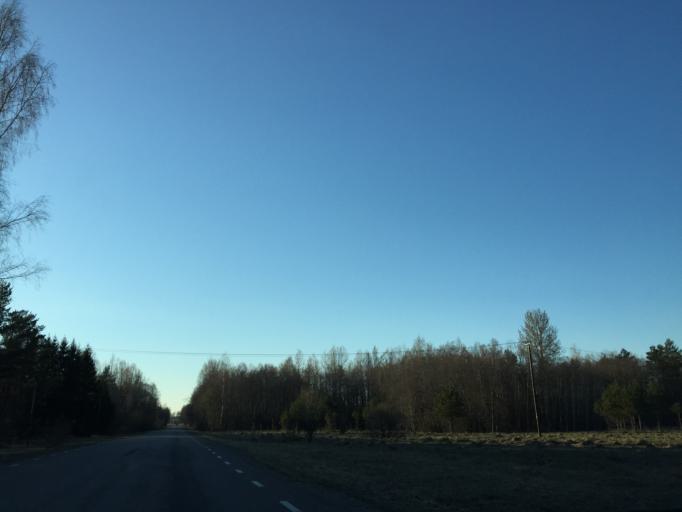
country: EE
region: Ida-Virumaa
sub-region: Sillamaee linn
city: Sillamae
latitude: 59.0877
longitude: 27.6669
